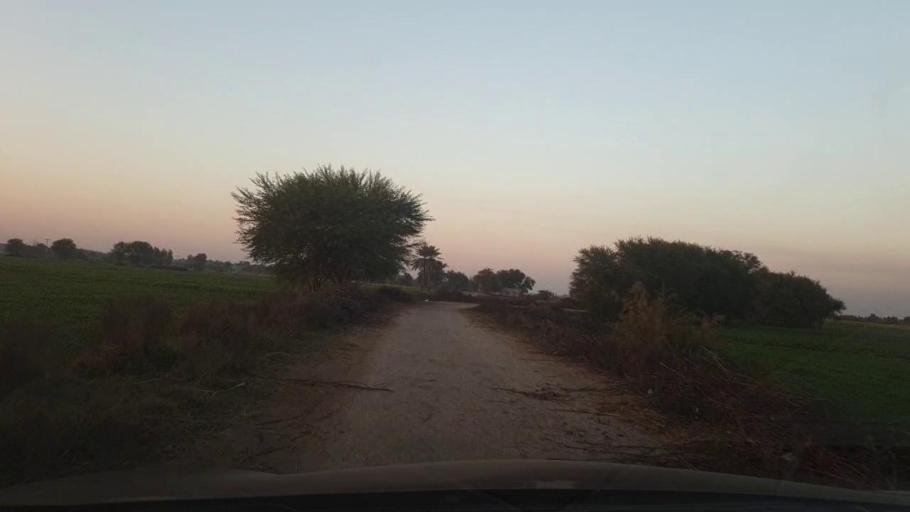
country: PK
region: Sindh
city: Ubauro
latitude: 28.1699
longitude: 69.6353
